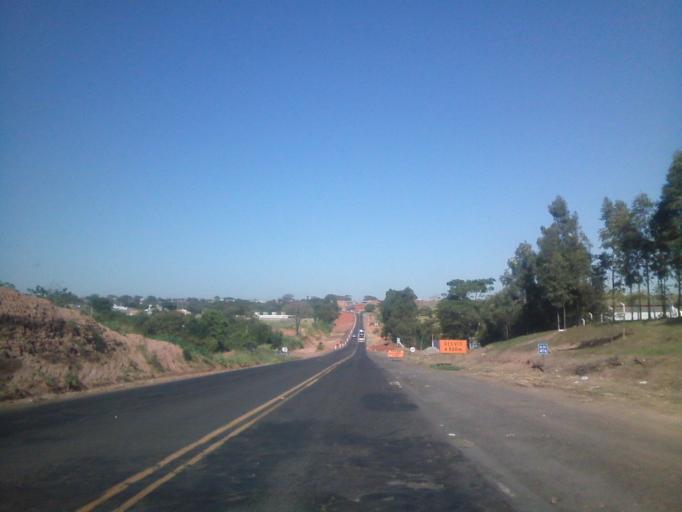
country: BR
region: Sao Paulo
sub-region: Pirapozinho
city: Pirapozinho
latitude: -22.2707
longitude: -51.5093
